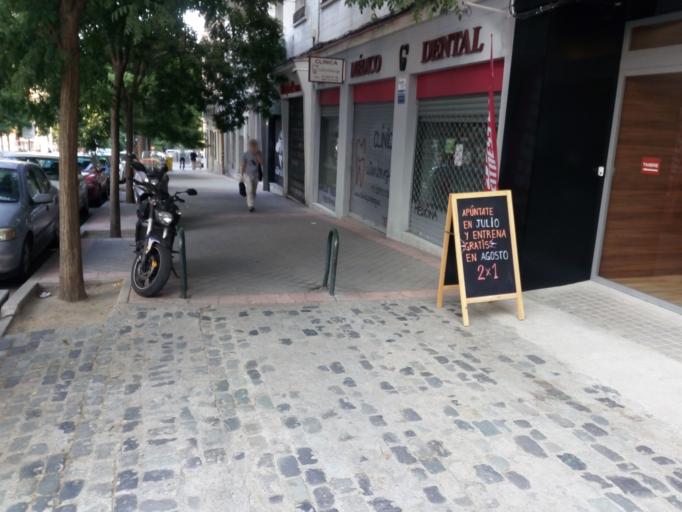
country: ES
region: Madrid
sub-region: Provincia de Madrid
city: Retiro
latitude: 40.4060
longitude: -3.6809
